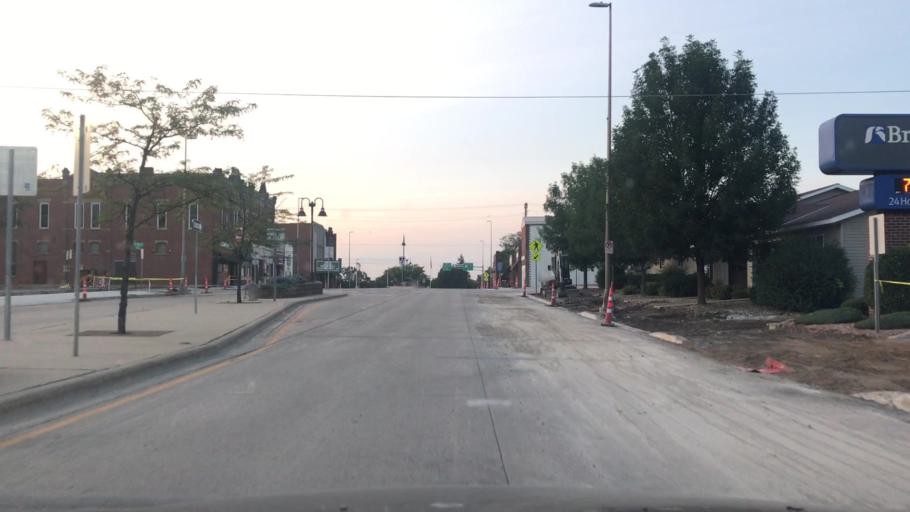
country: US
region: Minnesota
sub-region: Redwood County
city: Redwood Falls
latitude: 44.5389
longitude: -95.1194
